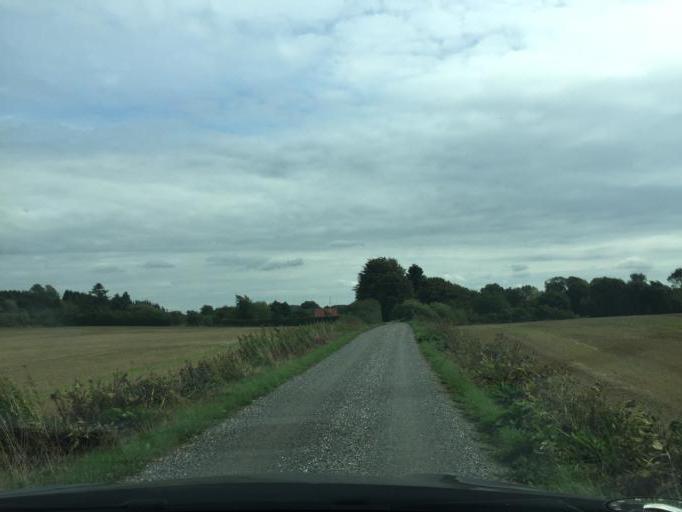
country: DK
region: South Denmark
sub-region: Assens Kommune
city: Vissenbjerg
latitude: 55.3617
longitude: 10.1487
